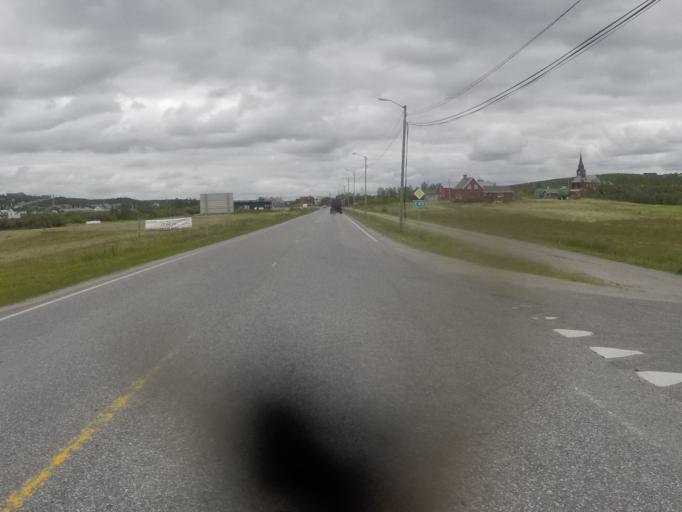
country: NO
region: Finnmark Fylke
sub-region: Kautokeino
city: Kautokeino
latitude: 69.0011
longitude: 23.0380
